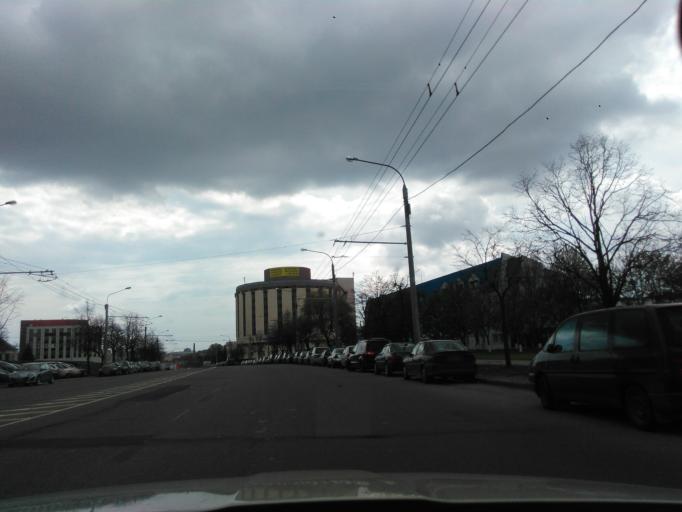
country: BY
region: Minsk
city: Minsk
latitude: 53.9025
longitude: 27.5338
